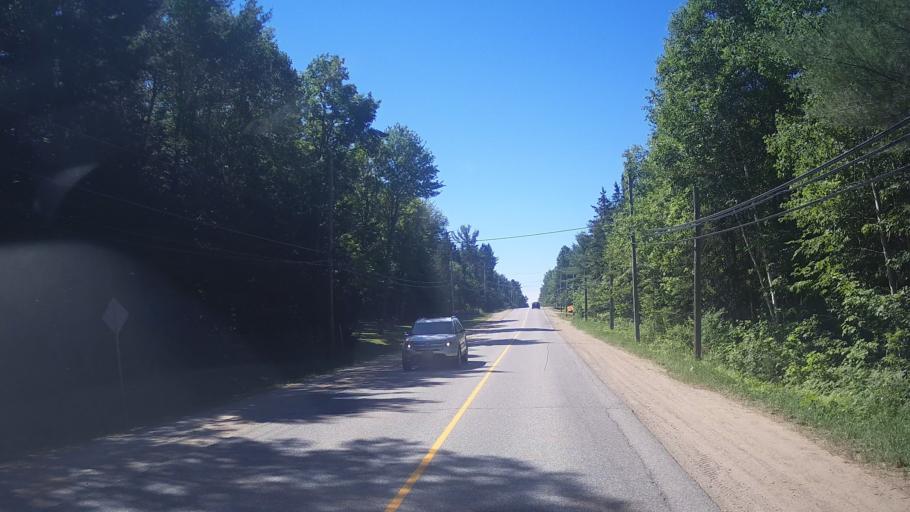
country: CA
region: Ontario
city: Huntsville
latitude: 45.3615
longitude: -79.2046
